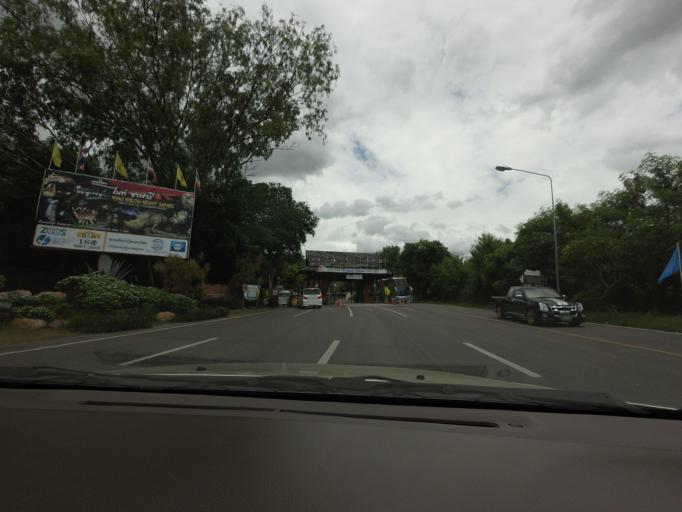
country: TH
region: Chon Buri
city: Ban Bueng
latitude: 13.2150
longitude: 101.0530
